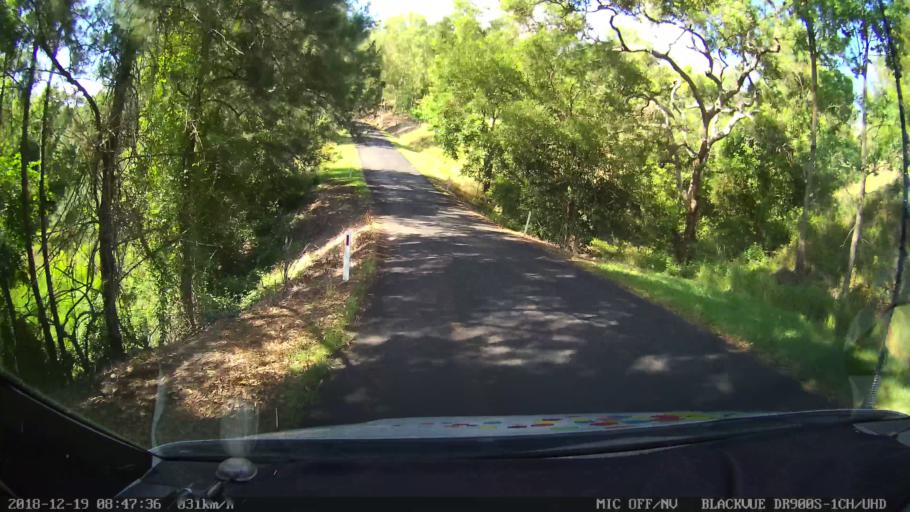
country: AU
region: New South Wales
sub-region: Kyogle
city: Kyogle
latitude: -28.3679
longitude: 152.9714
